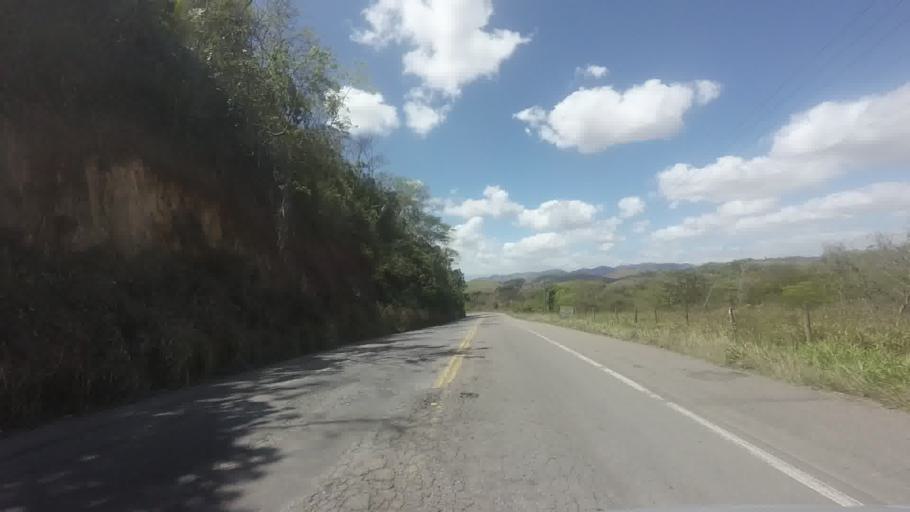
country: BR
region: Rio de Janeiro
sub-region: Santo Antonio De Padua
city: Santo Antonio de Padua
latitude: -21.6583
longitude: -42.3125
